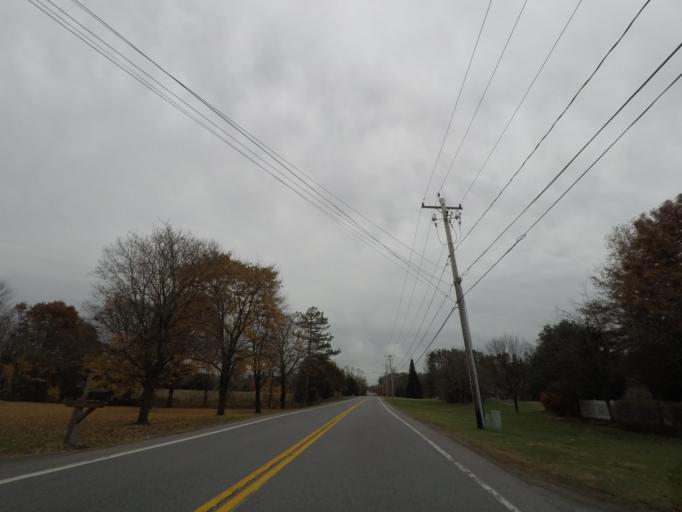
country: US
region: New York
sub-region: Saratoga County
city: Country Knolls
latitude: 42.8521
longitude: -73.8201
